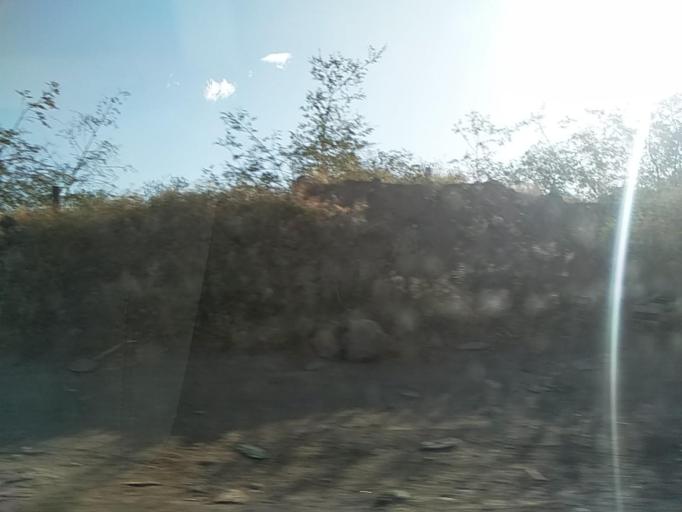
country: CL
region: Santiago Metropolitan
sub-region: Provincia de Chacabuco
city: Chicureo Abajo
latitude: -33.3090
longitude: -70.7157
